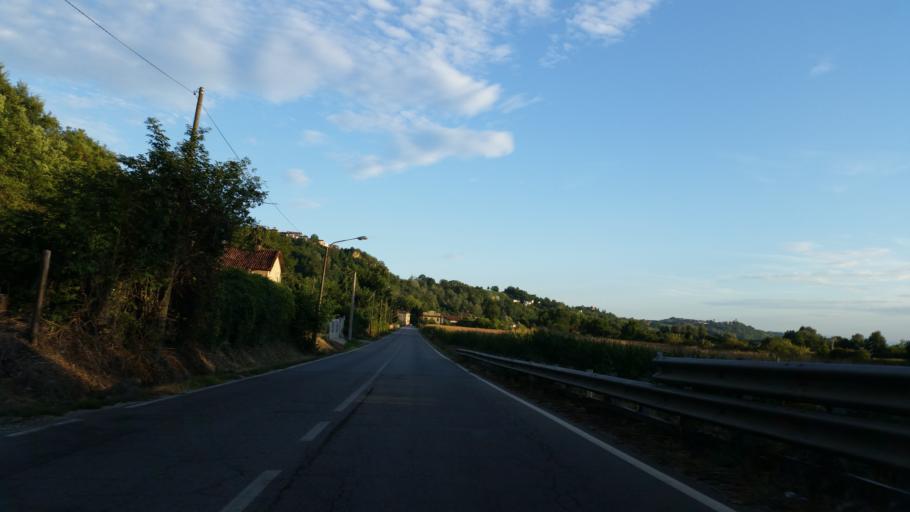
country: IT
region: Piedmont
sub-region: Provincia di Asti
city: Mongardino
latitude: 44.8716
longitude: 8.2090
